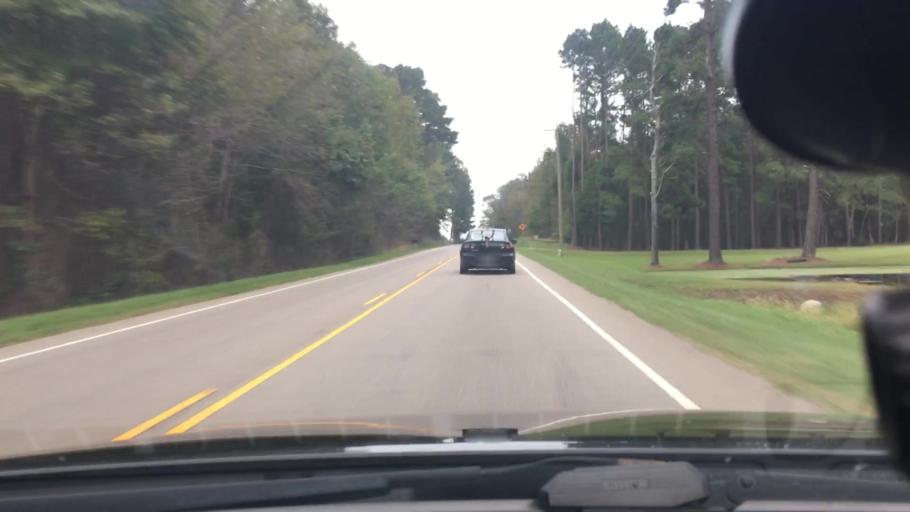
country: US
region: North Carolina
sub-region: Moore County
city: Robbins
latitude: 35.4020
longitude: -79.5571
